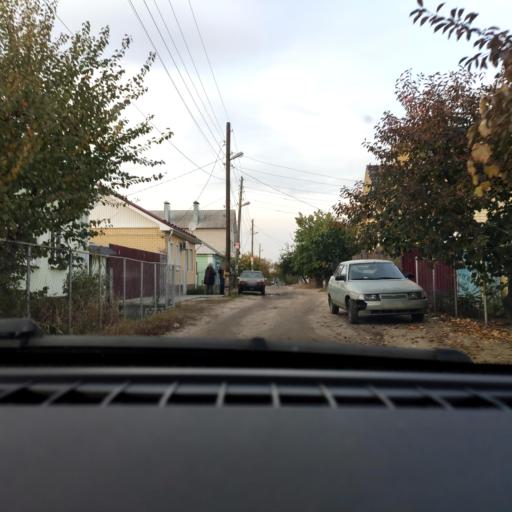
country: RU
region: Voronezj
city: Maslovka
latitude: 51.6075
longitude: 39.2330
